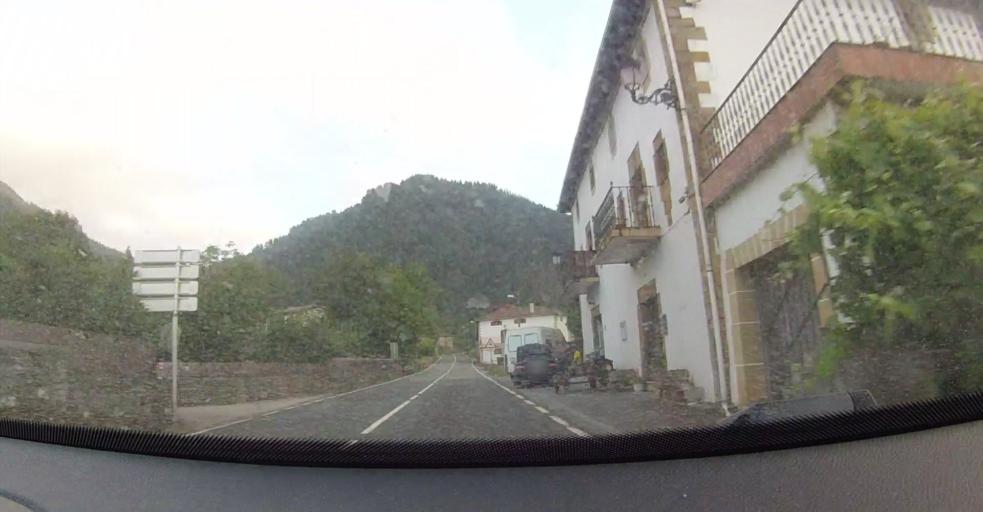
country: ES
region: Basque Country
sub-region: Bizkaia
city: Sopuerta
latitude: 43.2483
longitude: -3.1549
